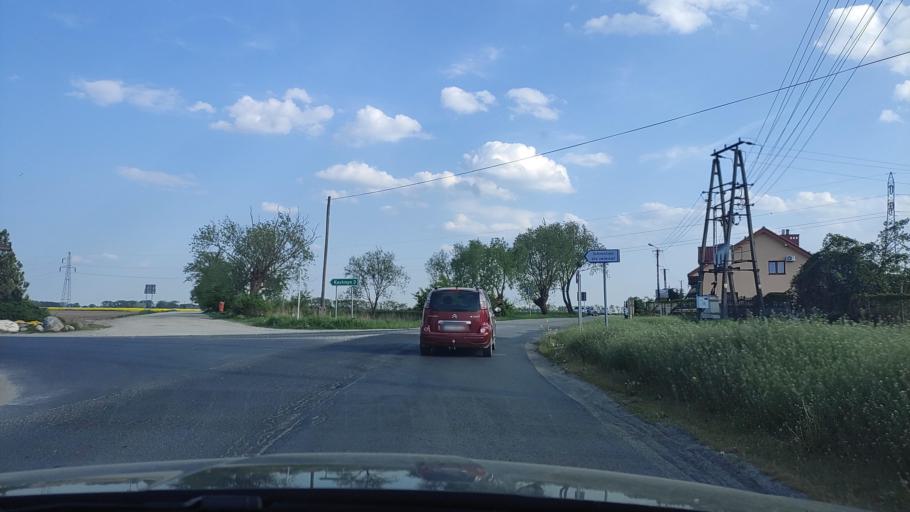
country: PL
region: Greater Poland Voivodeship
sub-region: Powiat poznanski
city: Kleszczewo
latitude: 52.3784
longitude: 17.1660
